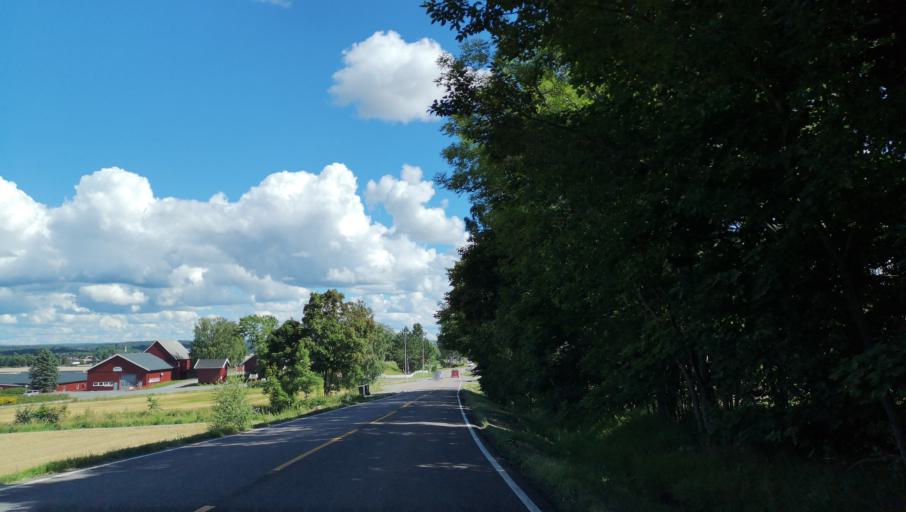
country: NO
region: Akershus
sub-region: Vestby
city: Vestby
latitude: 59.6584
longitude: 10.7123
